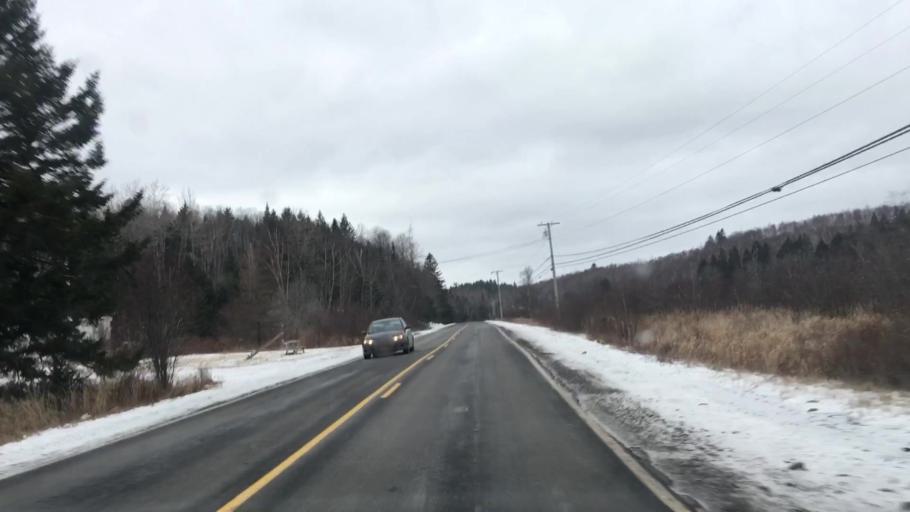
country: US
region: Maine
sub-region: Washington County
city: Machiasport
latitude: 44.7094
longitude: -67.3685
